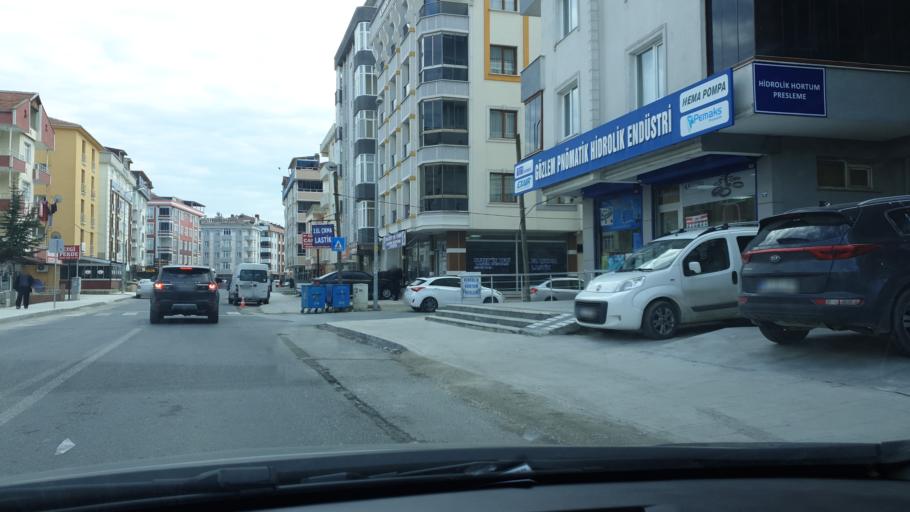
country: TR
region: Tekirdag
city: Cerkezkoey
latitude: 41.2875
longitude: 27.9923
